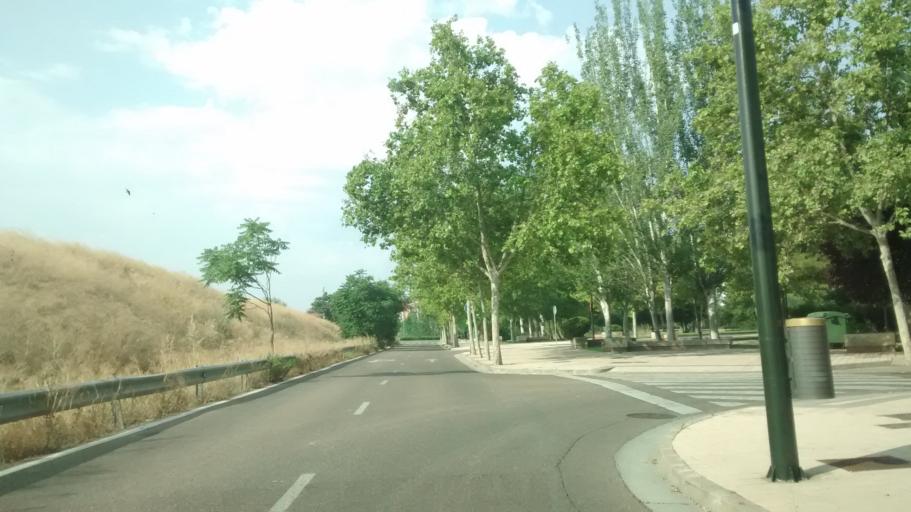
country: ES
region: Aragon
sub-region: Provincia de Zaragoza
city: Zaragoza
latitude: 41.6559
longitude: -0.8638
